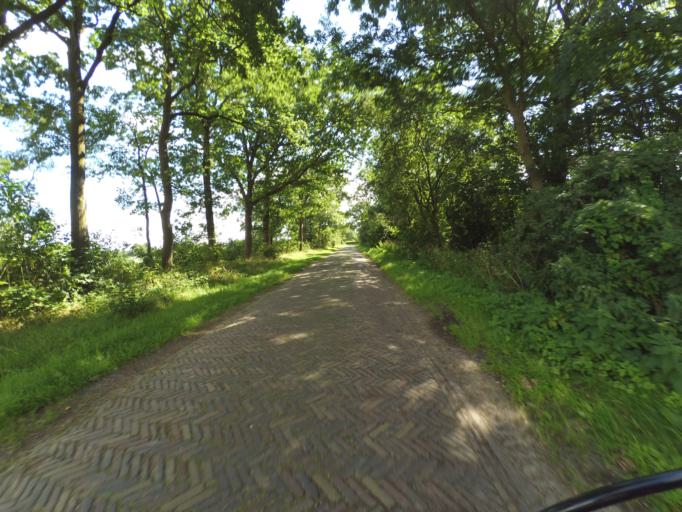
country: NL
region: Friesland
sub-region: Gemeente Achtkarspelen
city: Twijzelerheide
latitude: 53.2218
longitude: 6.0417
